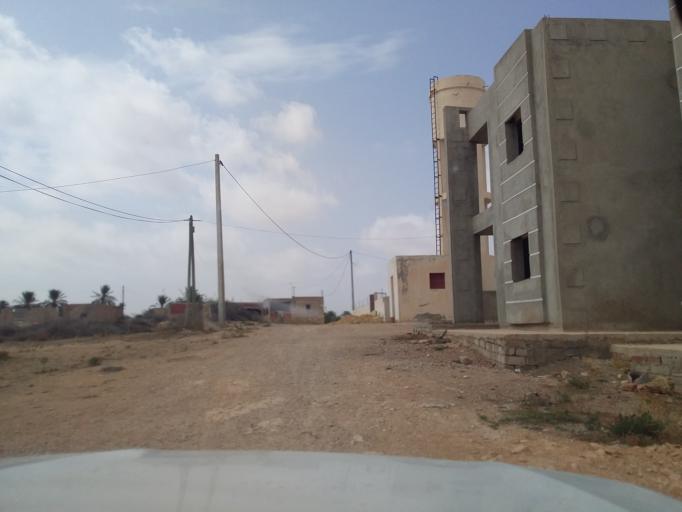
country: TN
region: Madanin
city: Medenine
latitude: 33.6237
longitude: 10.3126
